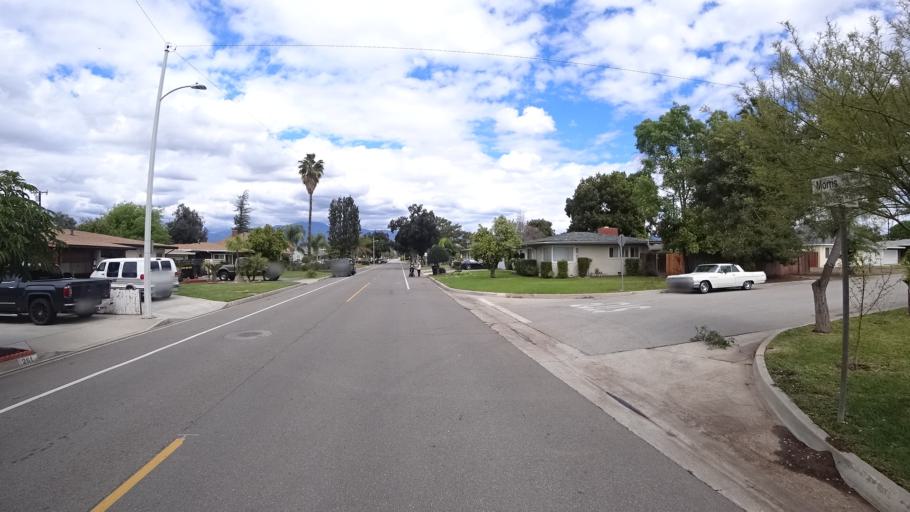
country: US
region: California
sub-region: Los Angeles County
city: West Covina
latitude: 34.0766
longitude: -117.9456
